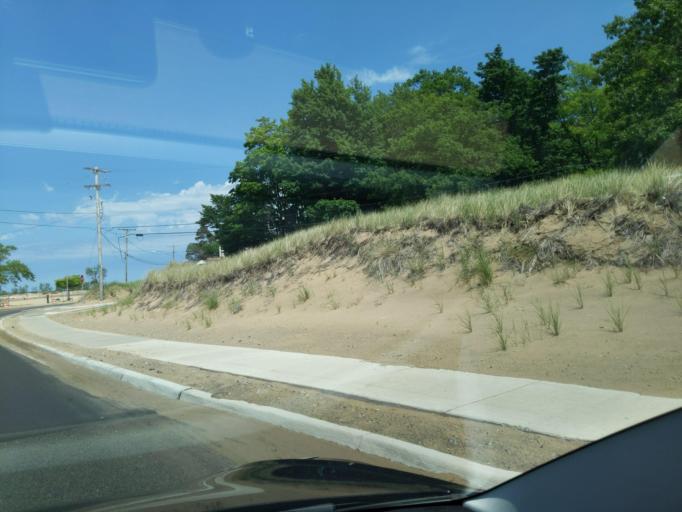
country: US
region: Michigan
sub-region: Muskegon County
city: Roosevelt Park
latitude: 43.2200
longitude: -86.3313
